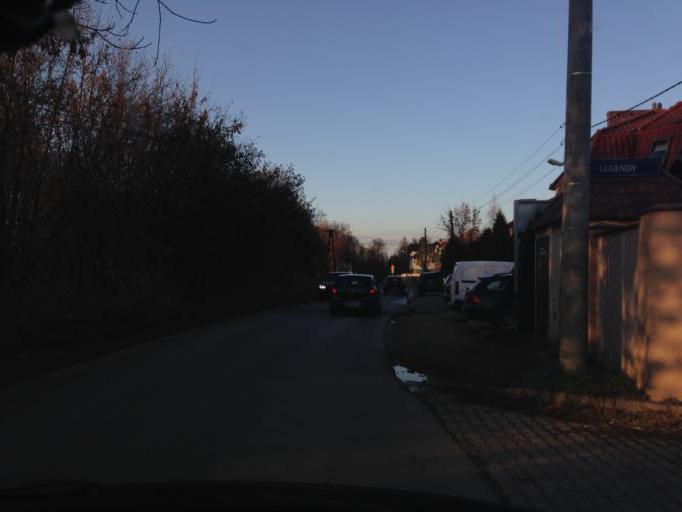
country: PL
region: Lesser Poland Voivodeship
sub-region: Powiat krakowski
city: Rzaska
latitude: 50.0721
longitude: 19.8777
